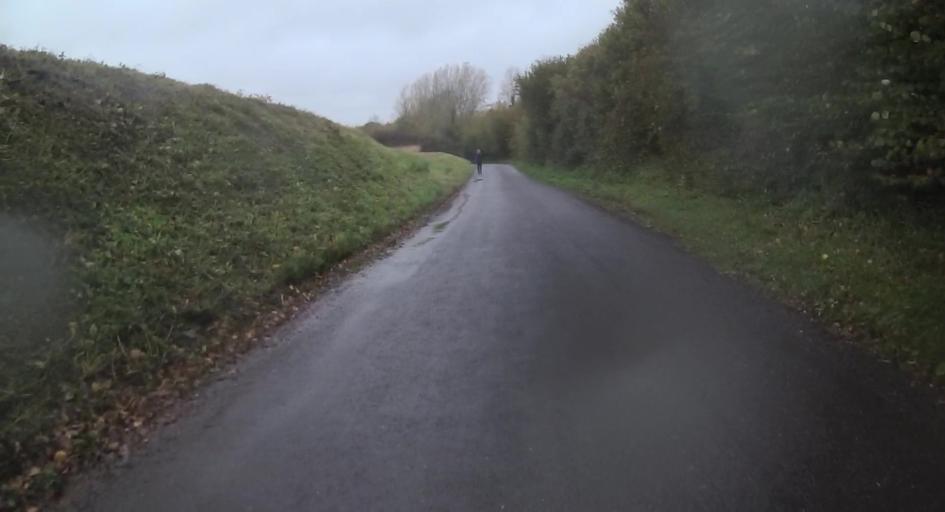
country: GB
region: England
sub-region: Hampshire
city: Kingsley
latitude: 51.1710
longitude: -0.8991
